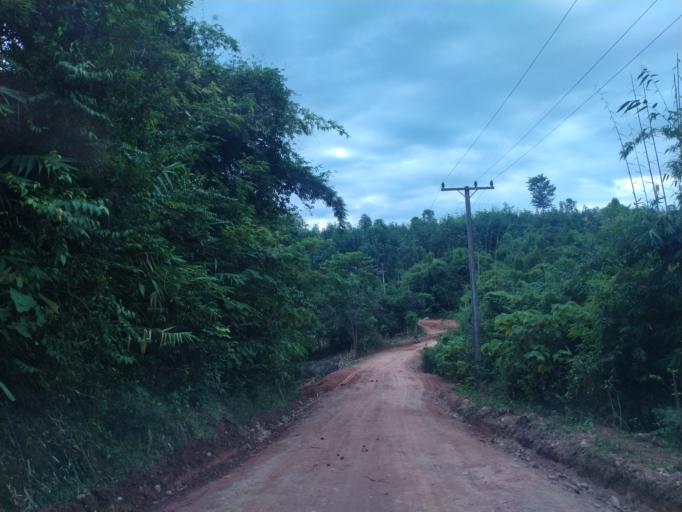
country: TH
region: Nong Khai
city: Rattanawapi
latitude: 18.5431
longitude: 102.9029
